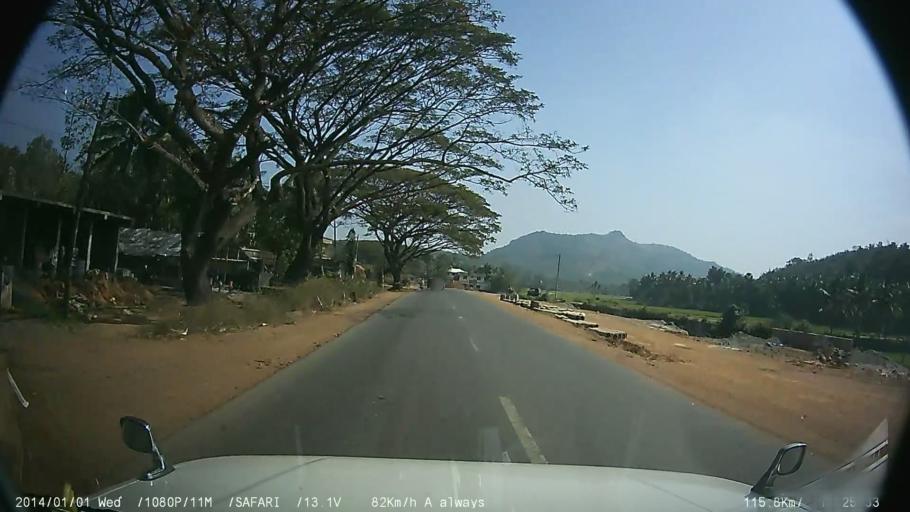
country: IN
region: Kerala
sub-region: Thrissur District
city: Chelakara
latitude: 10.6210
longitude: 76.5089
